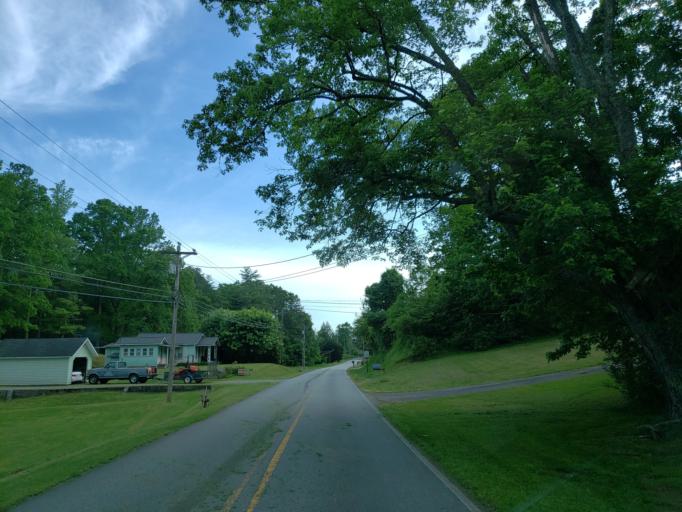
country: US
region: Georgia
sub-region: Fannin County
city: Blue Ridge
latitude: 34.8386
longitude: -84.3450
